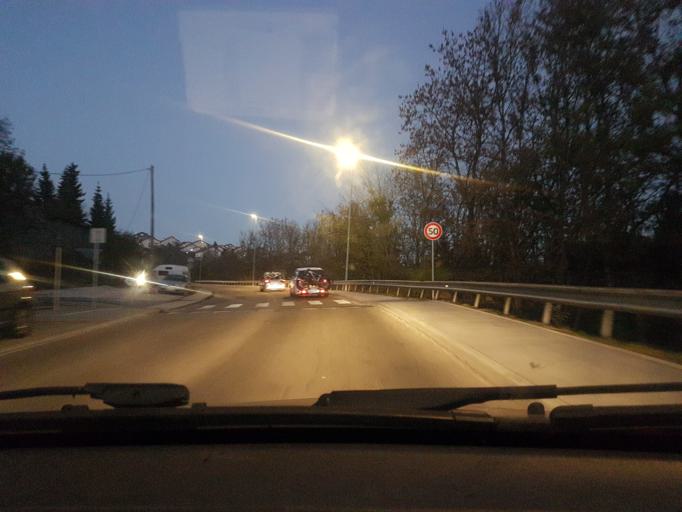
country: FR
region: Franche-Comte
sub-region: Departement du Doubs
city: Les Fins
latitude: 47.0802
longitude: 6.6281
